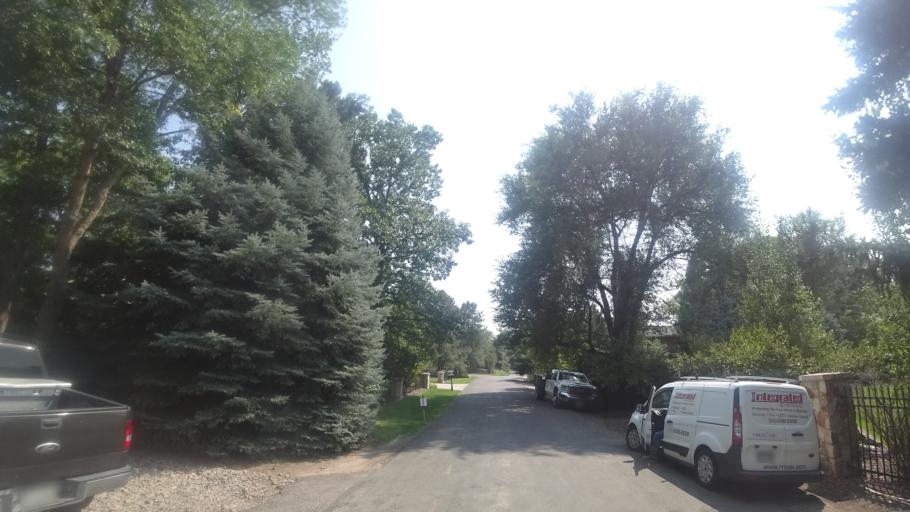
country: US
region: Colorado
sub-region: Arapahoe County
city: Cherry Hills Village
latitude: 39.6266
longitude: -104.9715
